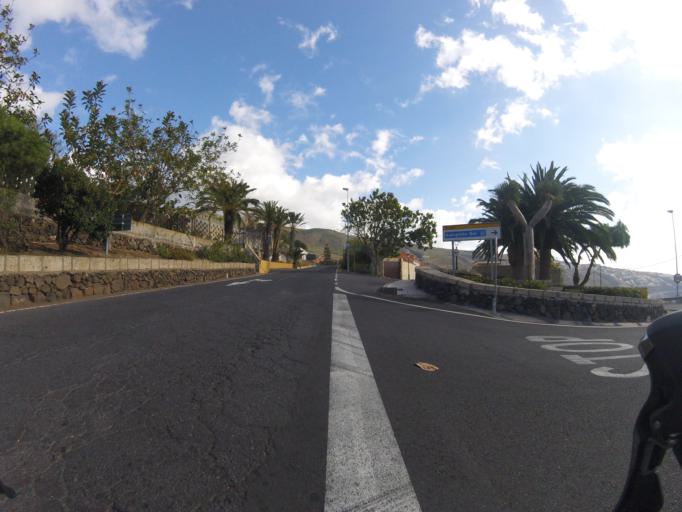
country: ES
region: Canary Islands
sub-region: Provincia de Santa Cruz de Tenerife
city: Candelaria
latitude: 28.3957
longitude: -16.3507
